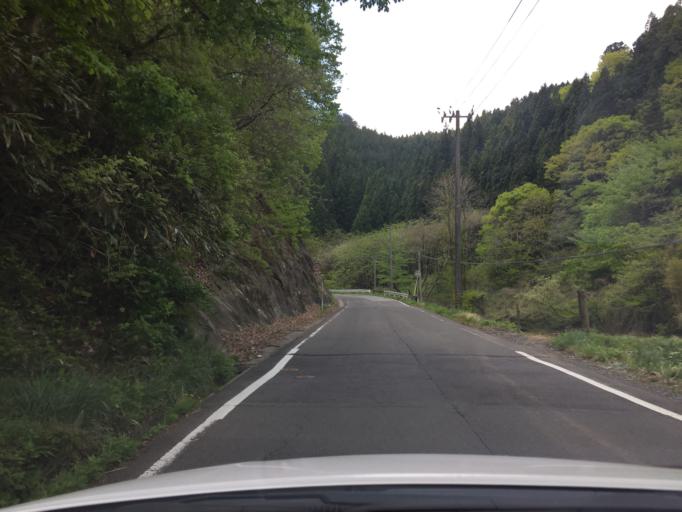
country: JP
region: Fukushima
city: Hobaramachi
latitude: 37.7298
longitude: 140.6398
